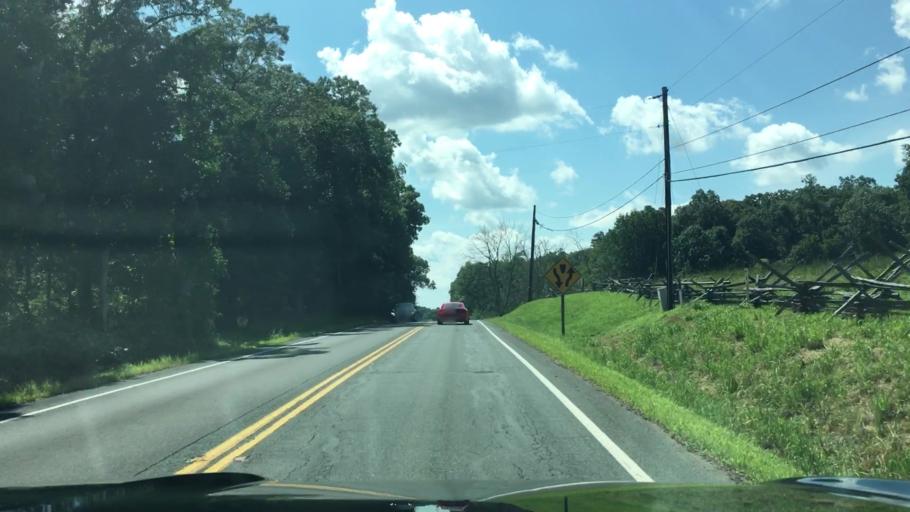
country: US
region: Virginia
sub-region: Prince William County
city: Bull Run
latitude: 38.8108
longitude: -77.5565
